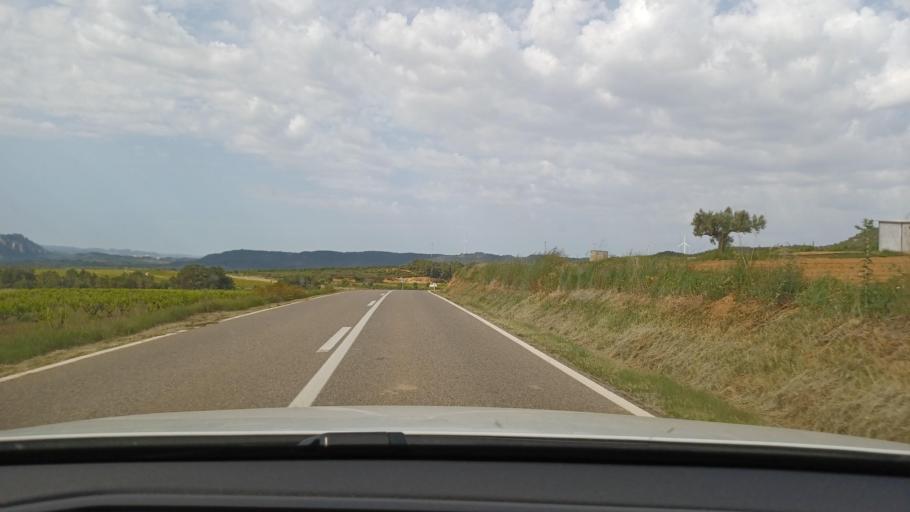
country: ES
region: Catalonia
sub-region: Provincia de Tarragona
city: Bot
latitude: 41.0390
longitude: 0.3835
